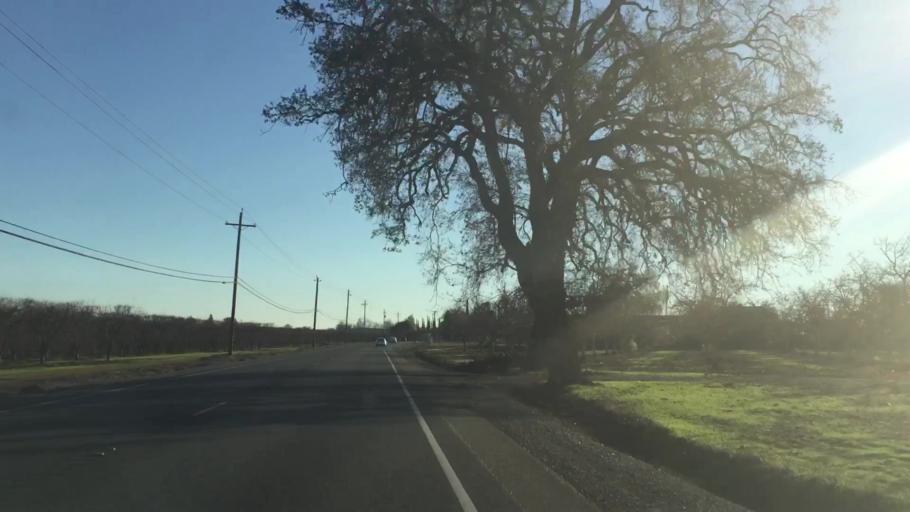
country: US
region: California
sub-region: Sutter County
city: Live Oak
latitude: 39.2901
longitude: -121.5949
